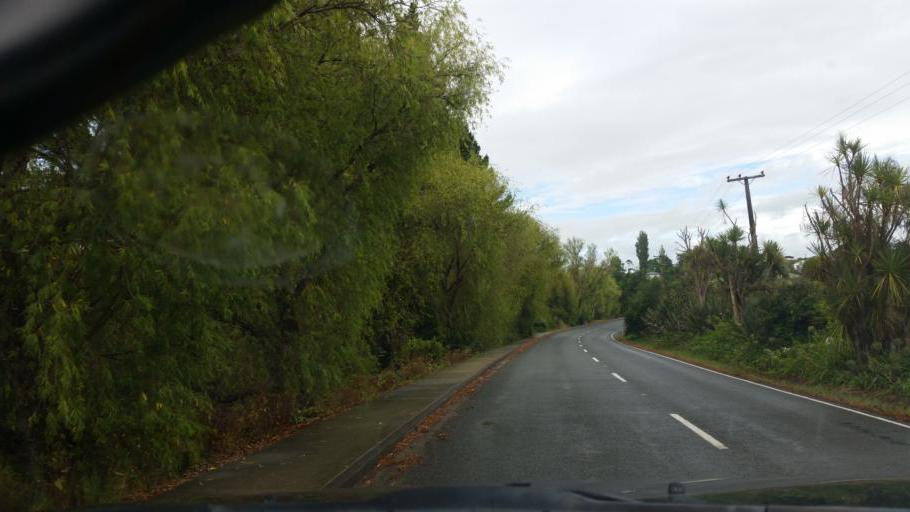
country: NZ
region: Northland
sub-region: Whangarei
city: Ruakaka
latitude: -36.1107
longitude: 174.3629
